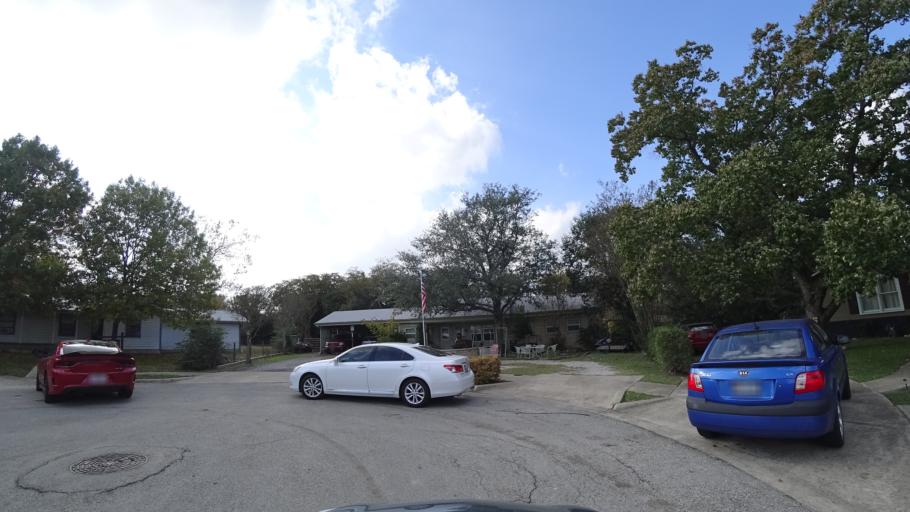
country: US
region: Texas
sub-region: Williamson County
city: Round Rock
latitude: 30.5130
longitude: -97.6739
